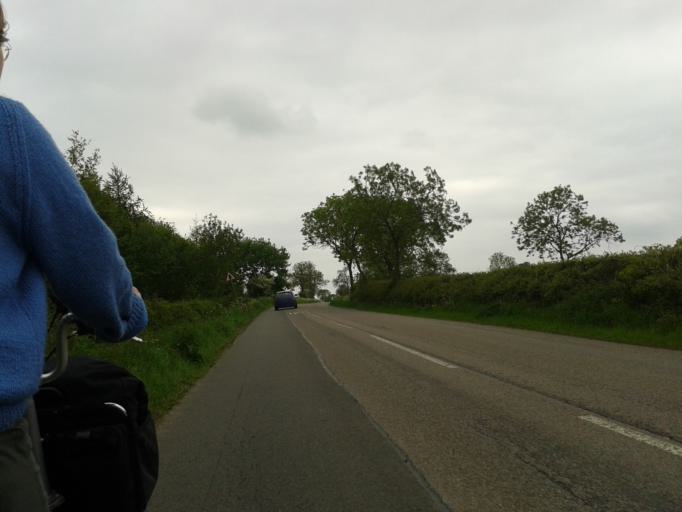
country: GB
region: England
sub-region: Leicestershire
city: Great Glen
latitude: 52.5167
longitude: -1.0591
